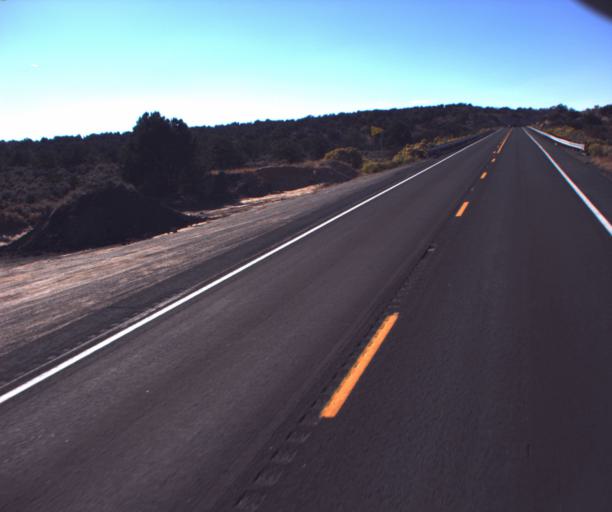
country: US
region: Arizona
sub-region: Coconino County
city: Kaibito
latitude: 36.5910
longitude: -110.8901
